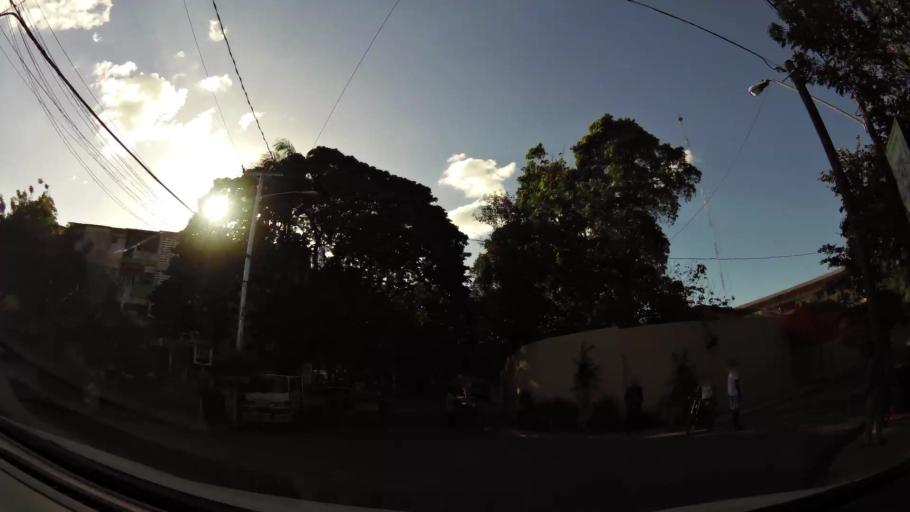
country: DO
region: Nacional
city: Santo Domingo
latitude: 18.4978
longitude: -69.9638
